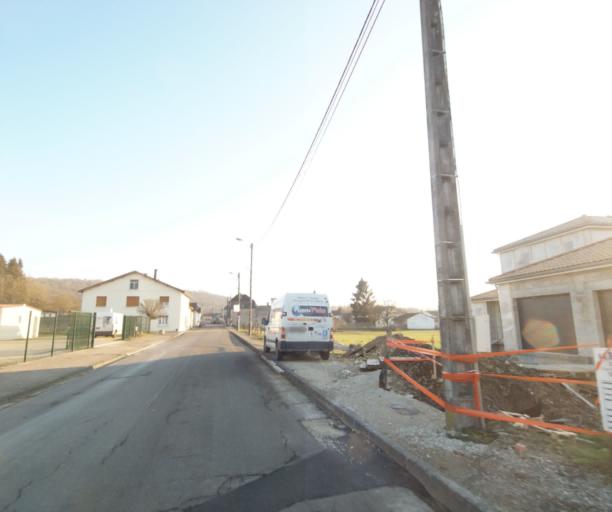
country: FR
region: Champagne-Ardenne
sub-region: Departement de la Haute-Marne
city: Chevillon
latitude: 48.5414
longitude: 5.1027
